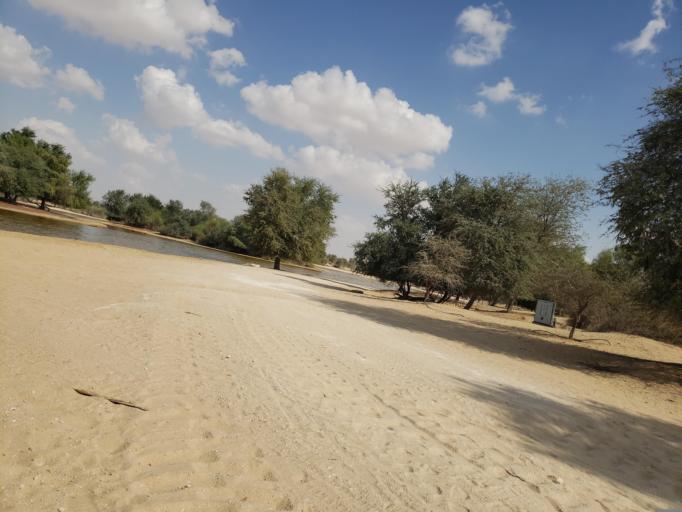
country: AE
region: Dubai
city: Dubai
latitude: 24.8336
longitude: 55.3779
